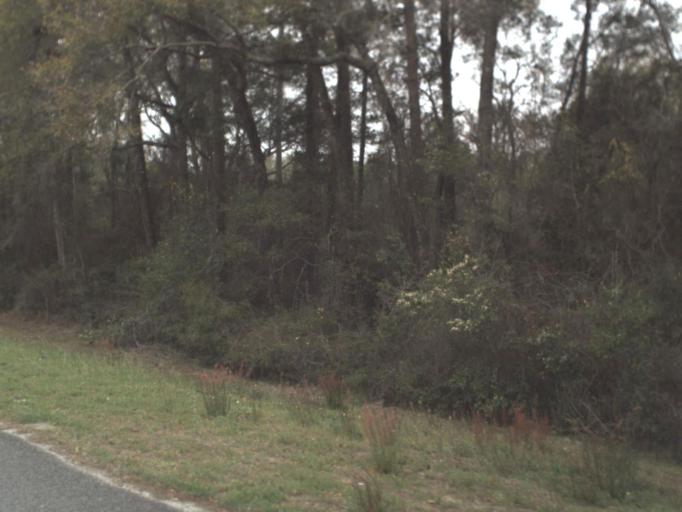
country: US
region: Florida
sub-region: Wakulla County
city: Crawfordville
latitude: 30.1457
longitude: -84.2957
